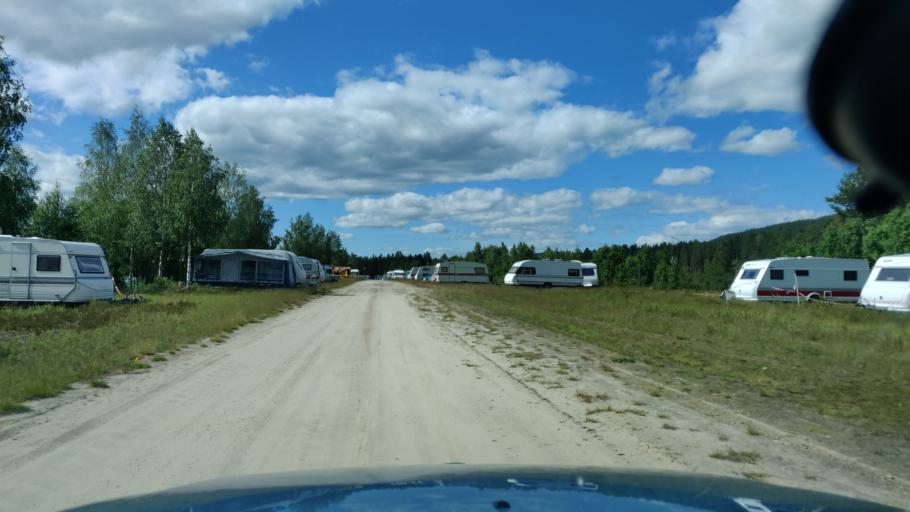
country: NO
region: Hedmark
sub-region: Trysil
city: Innbygda
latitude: 60.9094
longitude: 12.5662
